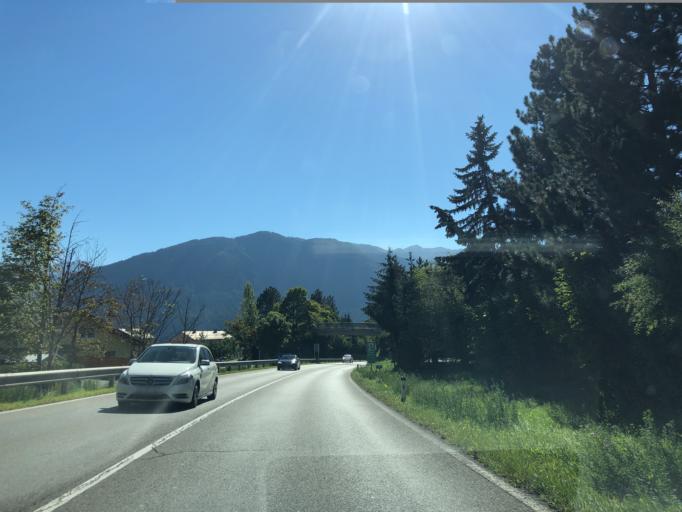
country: AT
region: Tyrol
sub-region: Politischer Bezirk Imst
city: Imst
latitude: 47.2453
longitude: 10.7452
